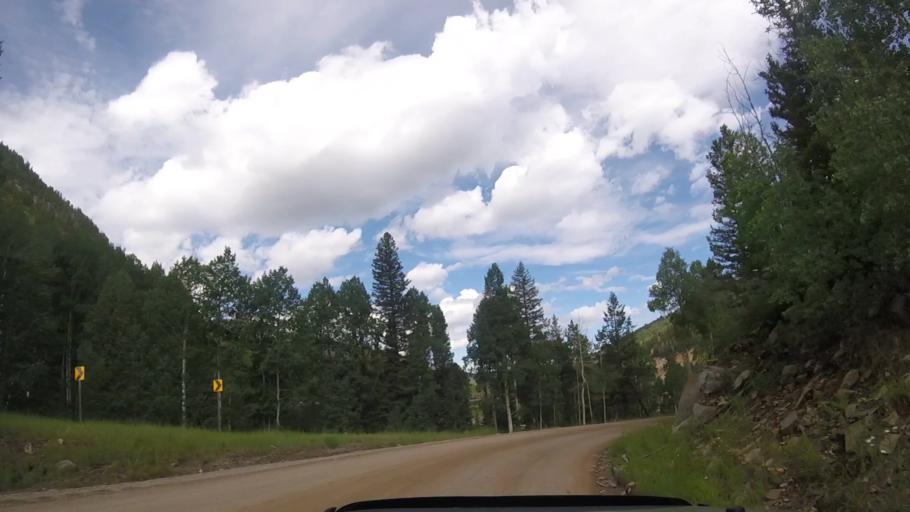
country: US
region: Colorado
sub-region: San Miguel County
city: Mountain Village
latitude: 37.8592
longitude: -107.8680
